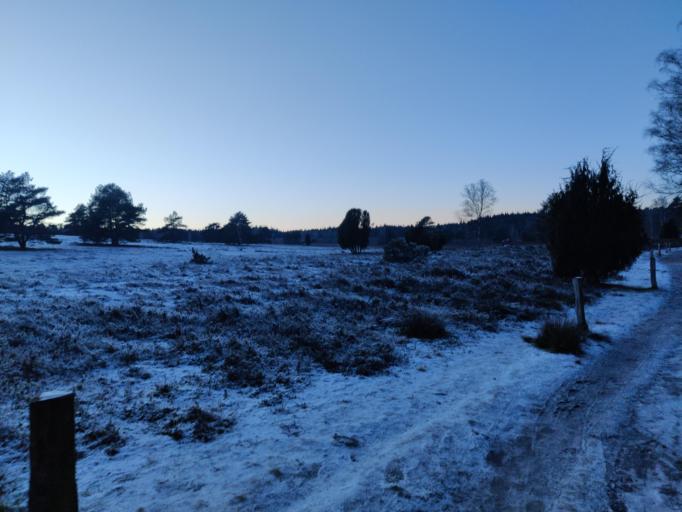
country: DE
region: Lower Saxony
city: Handeloh
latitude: 53.2726
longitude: 9.8459
